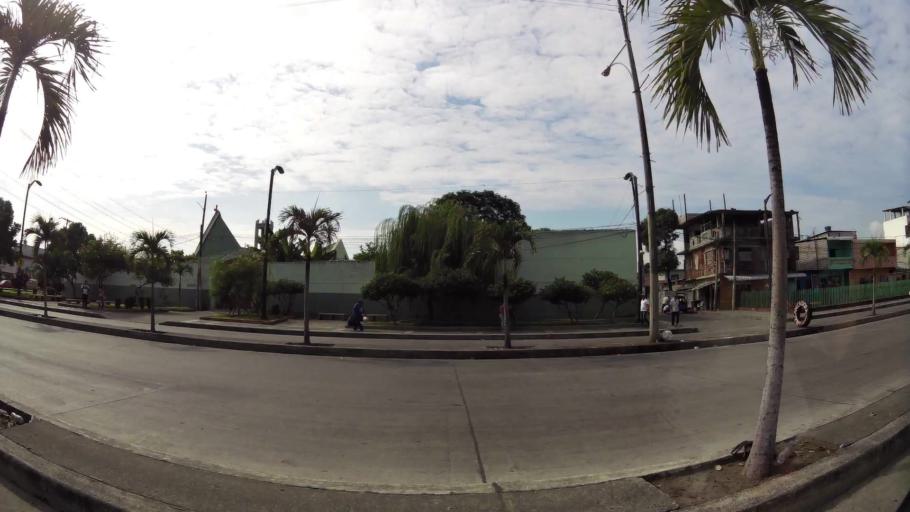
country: EC
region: Guayas
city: Guayaquil
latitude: -2.2591
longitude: -79.8899
